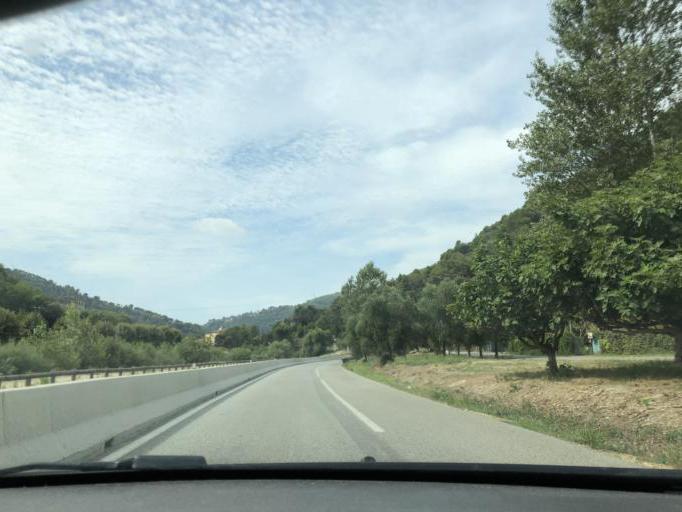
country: FR
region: Provence-Alpes-Cote d'Azur
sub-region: Departement des Alpes-Maritimes
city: Cantaron
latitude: 43.7744
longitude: 7.3349
